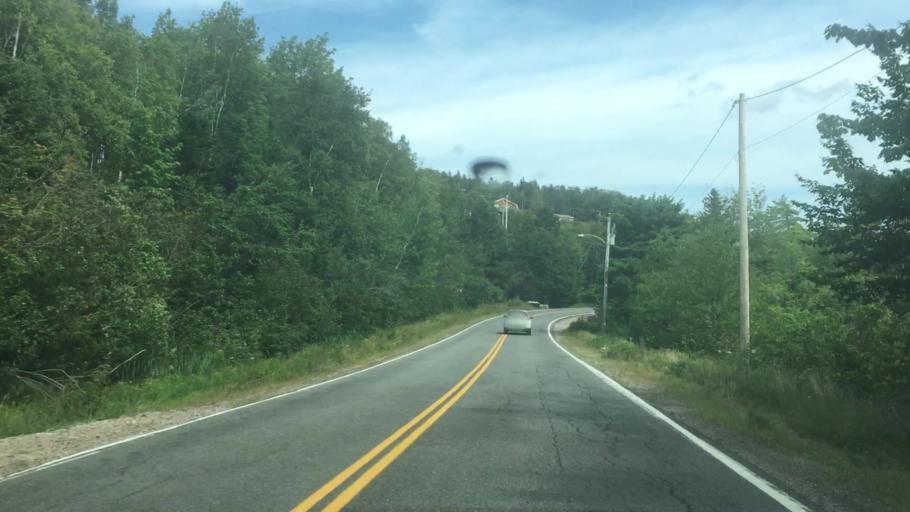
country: CA
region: Nova Scotia
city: Sydney Mines
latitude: 46.6356
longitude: -60.4213
